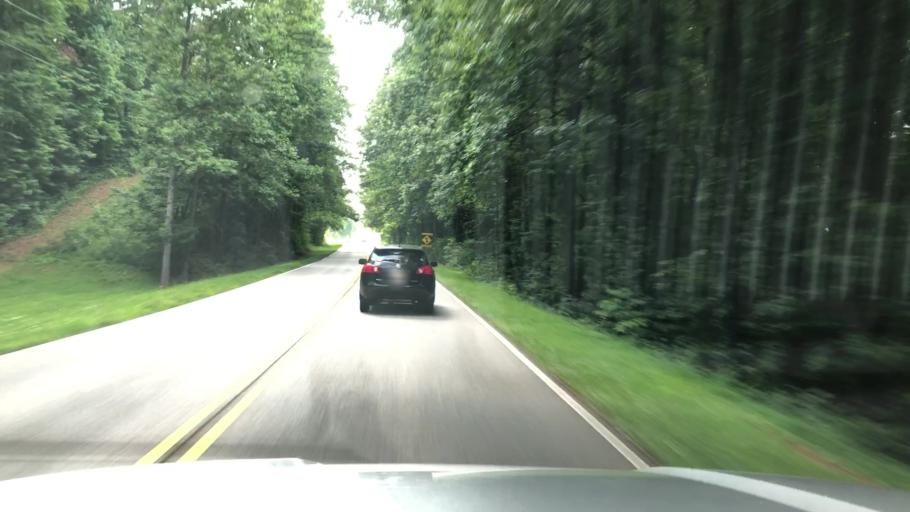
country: US
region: Georgia
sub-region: Paulding County
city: Dallas
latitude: 33.9543
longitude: -84.7807
